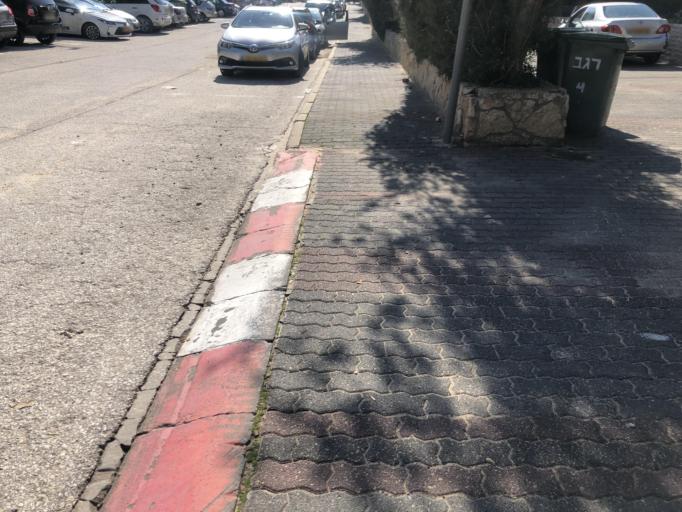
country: PS
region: West Bank
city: Az Zawiyah
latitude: 32.1107
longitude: 35.0354
